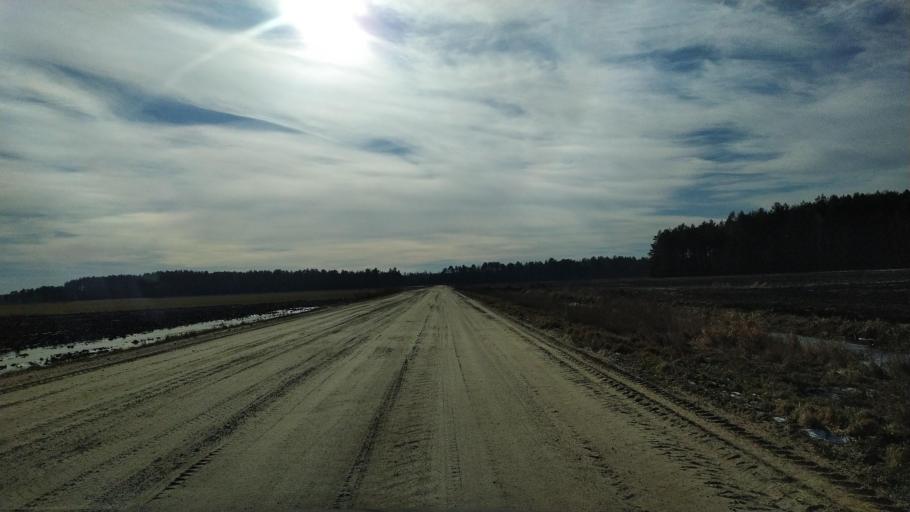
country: BY
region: Brest
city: Pruzhany
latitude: 52.5643
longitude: 24.2947
